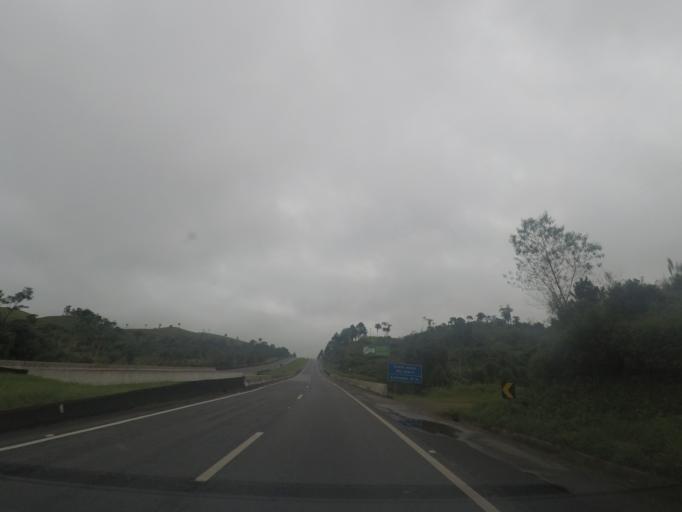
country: BR
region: Parana
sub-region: Antonina
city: Antonina
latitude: -25.0766
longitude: -48.5945
